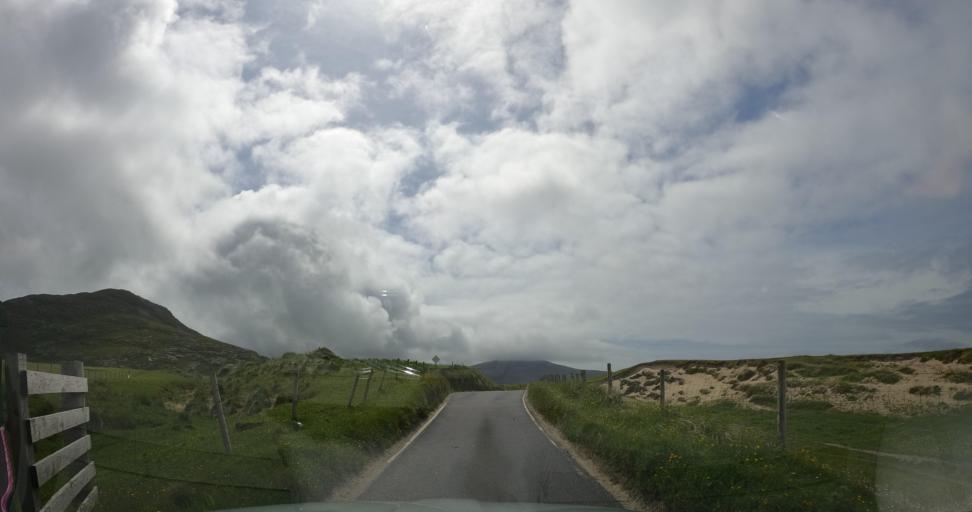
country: GB
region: Scotland
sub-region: Eilean Siar
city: Barra
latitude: 56.9990
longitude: -7.5049
